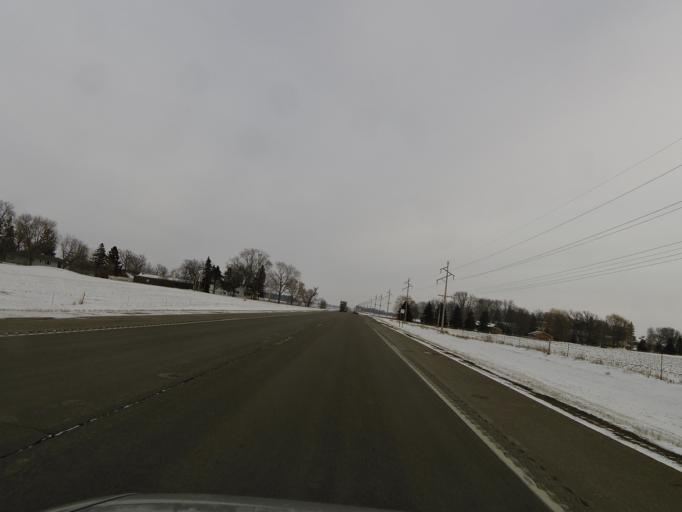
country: US
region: Minnesota
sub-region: Carver County
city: Mayer
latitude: 44.9059
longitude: -93.9431
